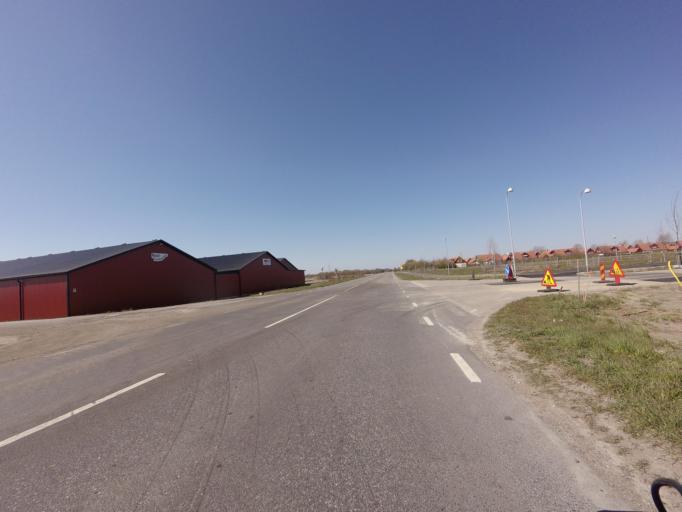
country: SE
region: Skane
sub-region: Vellinge Kommun
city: Vellinge
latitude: 55.4709
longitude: 13.0430
